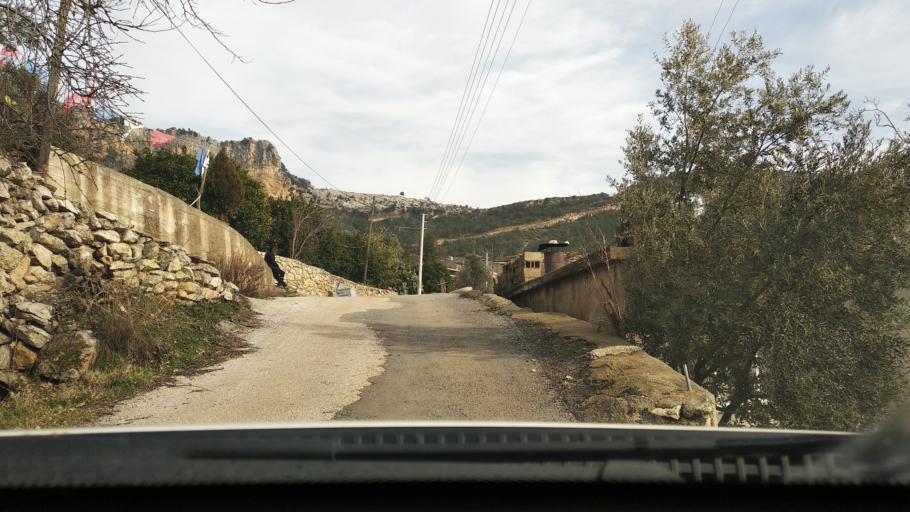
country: TR
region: Mersin
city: Kuzucubelen
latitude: 36.8777
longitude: 34.4689
